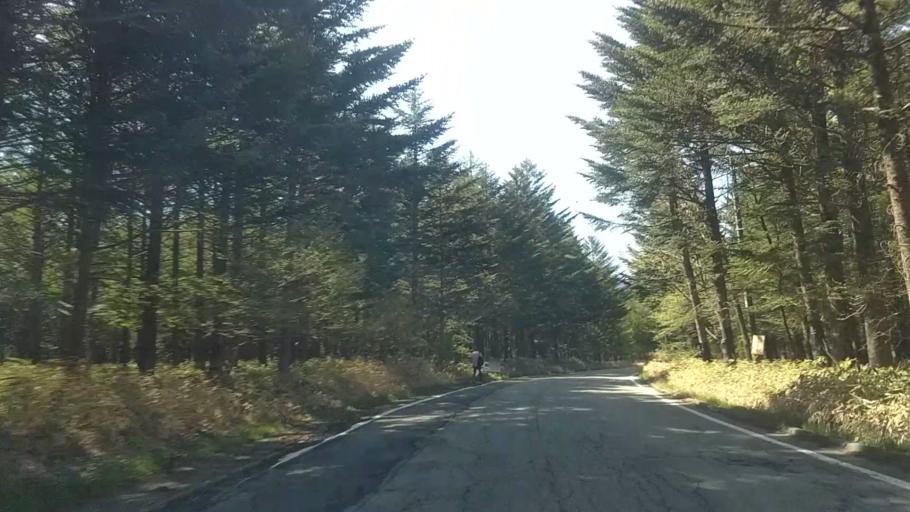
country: JP
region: Yamanashi
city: Nirasaki
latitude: 35.9406
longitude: 138.4214
